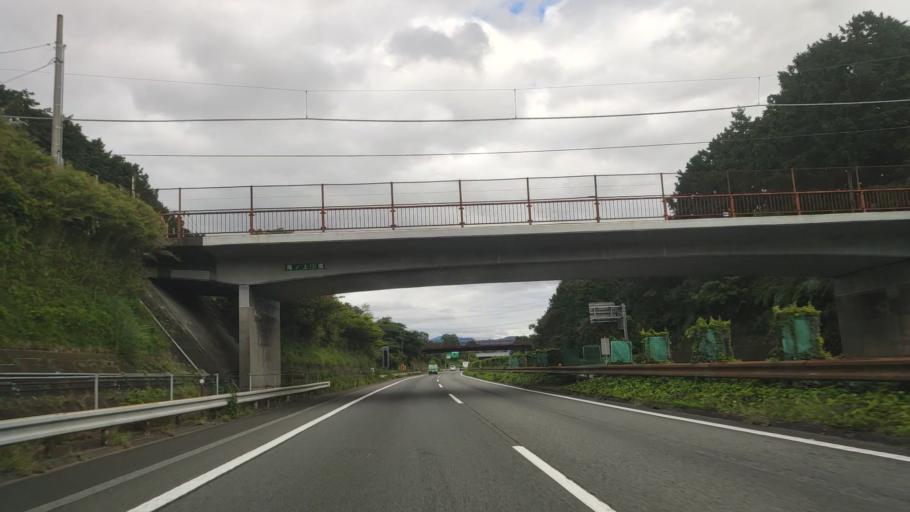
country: JP
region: Shizuoka
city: Numazu
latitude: 35.1446
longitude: 138.8480
